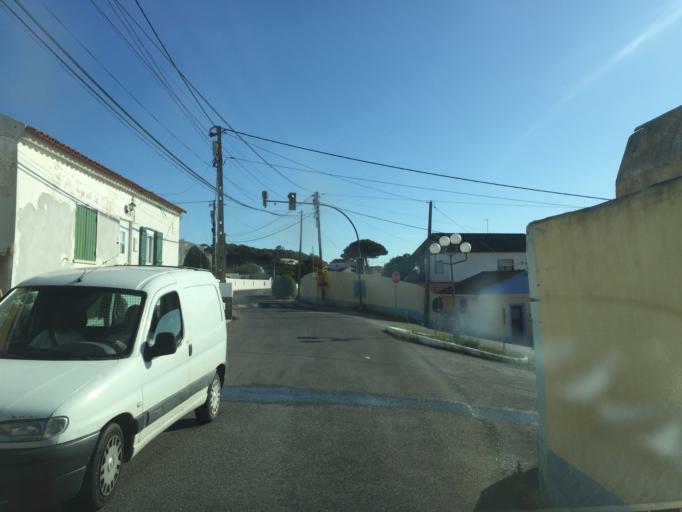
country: PT
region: Lisbon
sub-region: Torres Vedras
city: Torres Vedras
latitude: 39.0882
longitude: -9.2784
